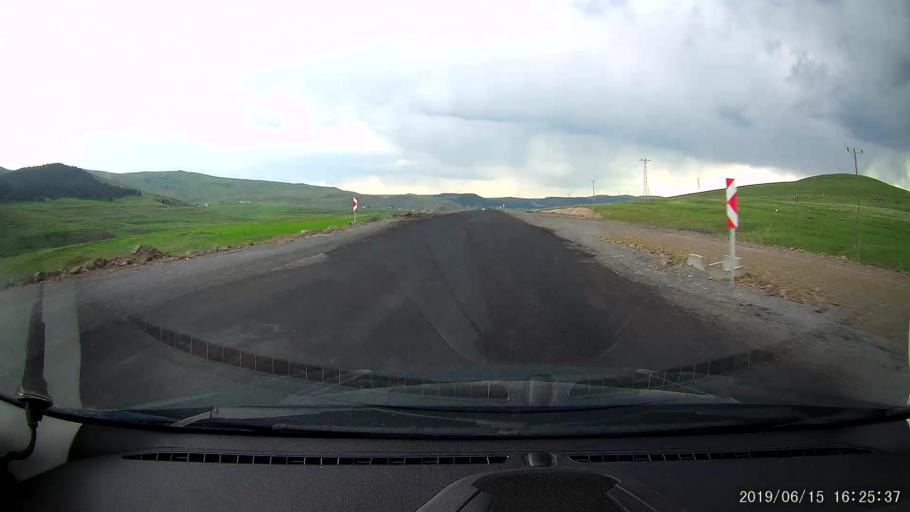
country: TR
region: Ardahan
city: Hanak
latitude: 41.1515
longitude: 42.8681
